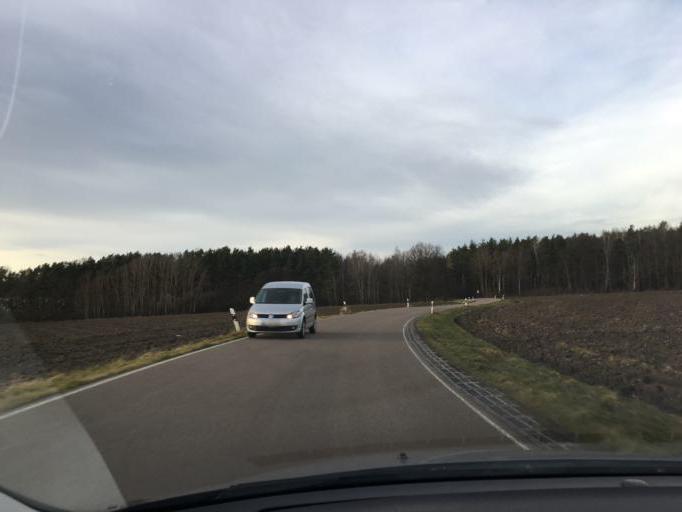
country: DE
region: Saxony
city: Belgershain
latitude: 51.2227
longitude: 12.5081
